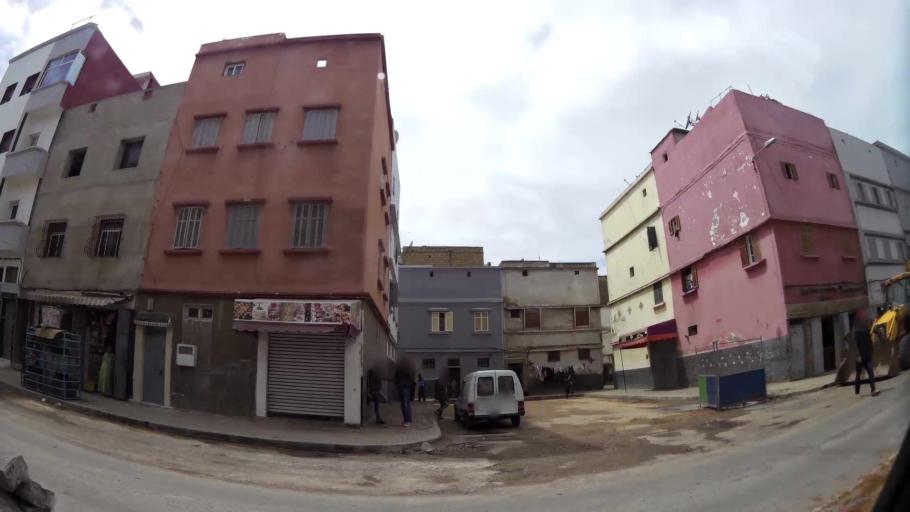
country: MA
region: Grand Casablanca
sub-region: Mediouna
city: Tit Mellil
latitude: 33.6062
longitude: -7.5048
